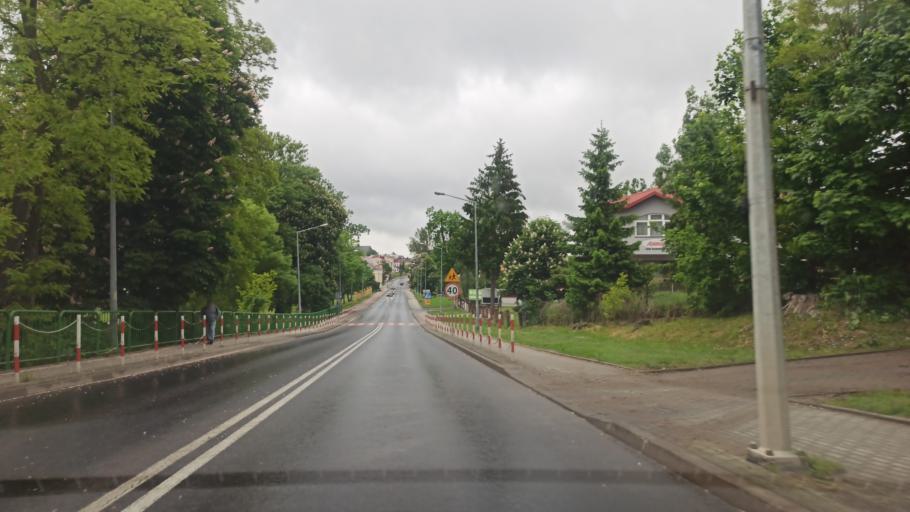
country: PL
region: Subcarpathian Voivodeship
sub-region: Powiat jaroslawski
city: Radymno
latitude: 49.9477
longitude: 22.8229
